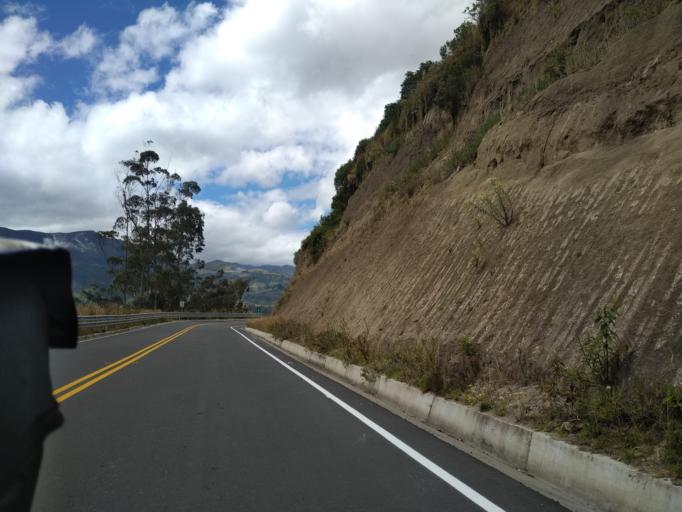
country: EC
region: Cotopaxi
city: Saquisili
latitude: -0.7248
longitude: -78.8920
